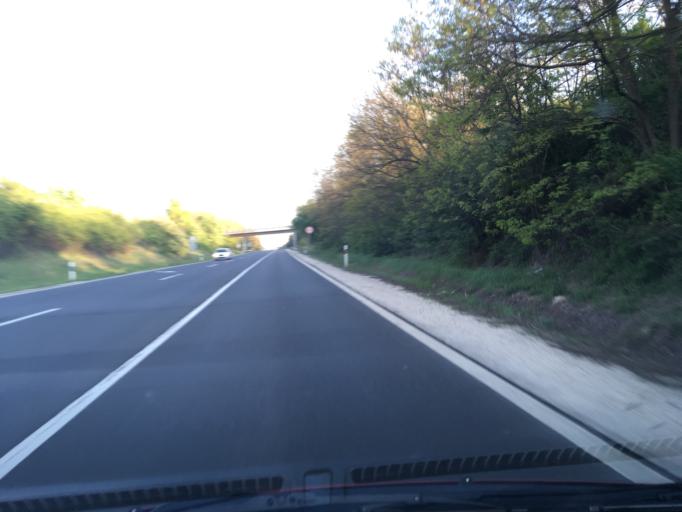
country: HU
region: Pest
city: Kosd
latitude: 47.7822
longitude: 19.1704
